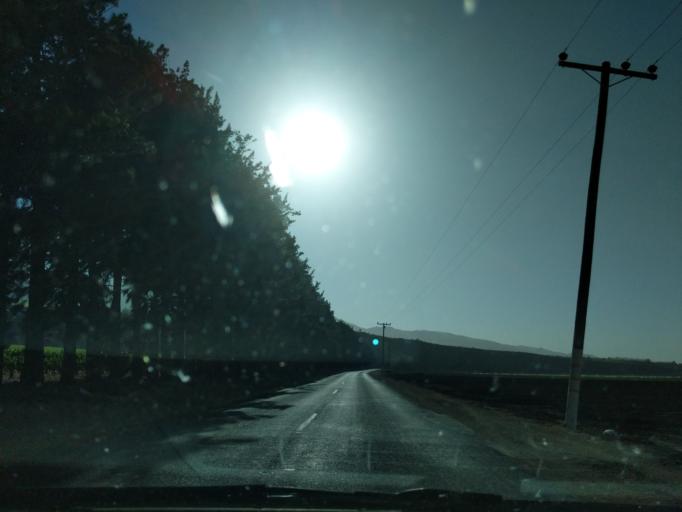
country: US
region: California
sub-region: Monterey County
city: Soledad
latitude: 36.4106
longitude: -121.3844
